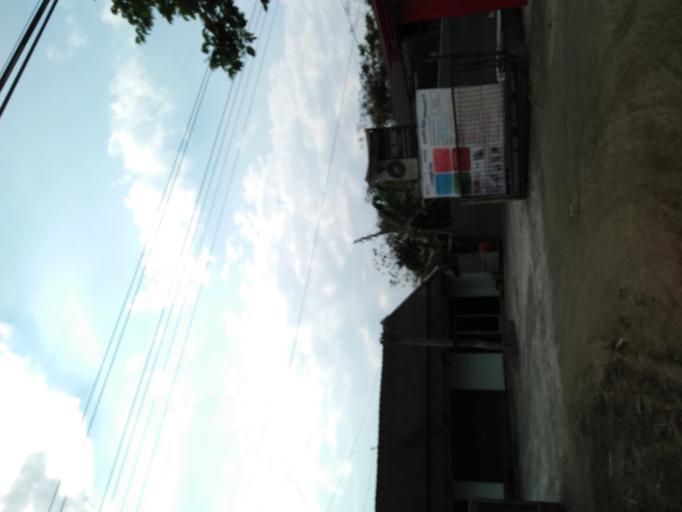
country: ID
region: Central Java
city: Candi Prambanan
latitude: -7.8226
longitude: 110.4801
